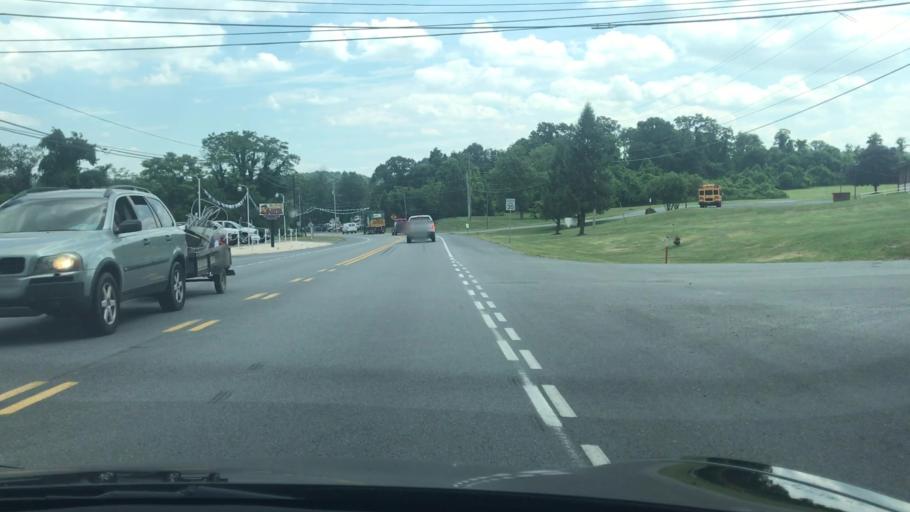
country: US
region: Pennsylvania
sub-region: York County
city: Valley Green
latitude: 40.1319
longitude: -76.8015
